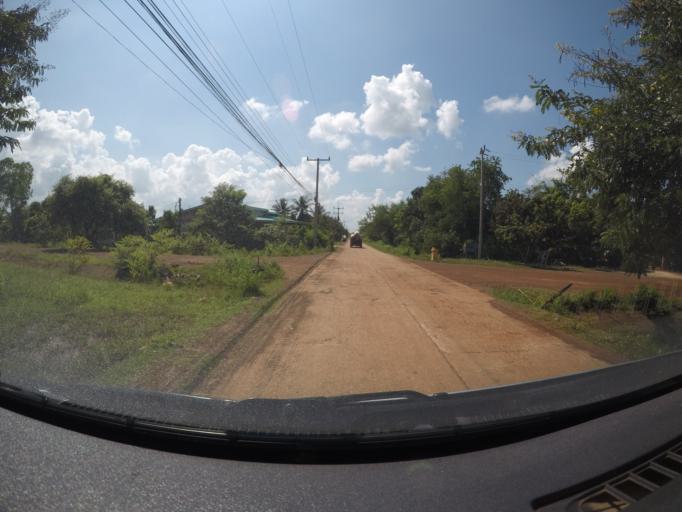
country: TH
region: Sakon Nakhon
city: Sakon Nakhon
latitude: 17.2106
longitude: 104.1281
